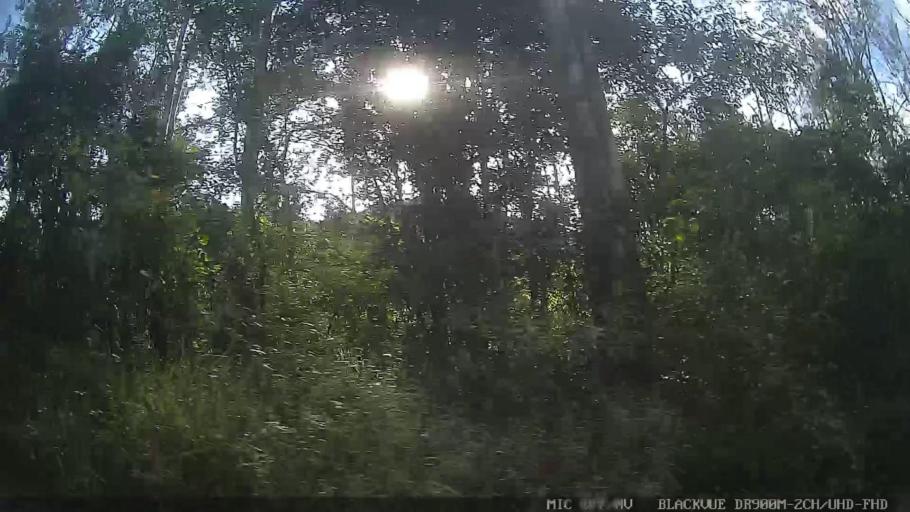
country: BR
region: Sao Paulo
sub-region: Bom Jesus Dos Perdoes
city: Bom Jesus dos Perdoes
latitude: -23.1608
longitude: -46.5113
